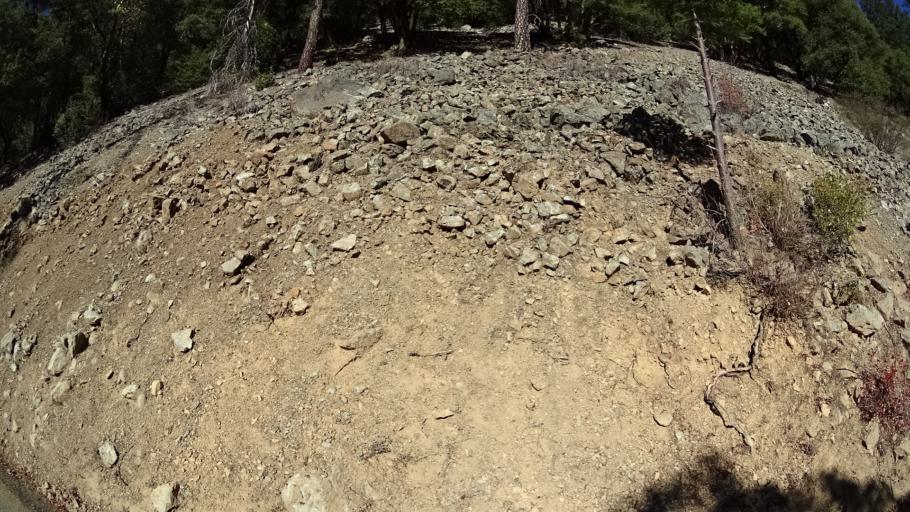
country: US
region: California
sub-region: Siskiyou County
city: Happy Camp
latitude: 41.2951
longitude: -123.1141
